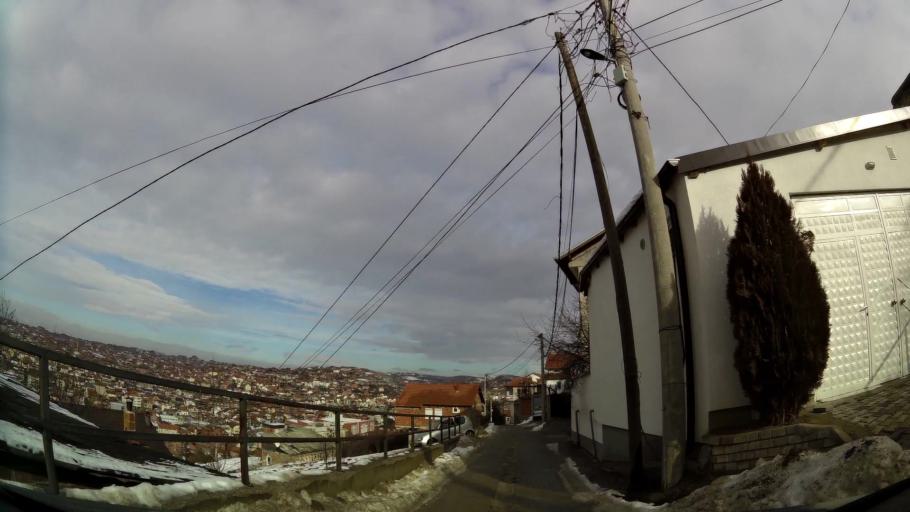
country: XK
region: Pristina
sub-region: Komuna e Prishtines
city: Pristina
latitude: 42.6745
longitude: 21.1761
